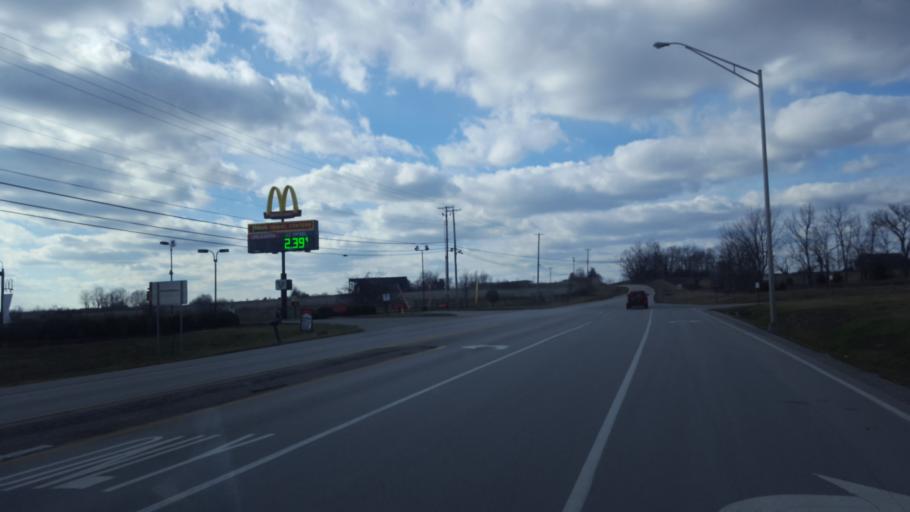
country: US
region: Kentucky
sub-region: Scott County
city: Georgetown
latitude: 38.2771
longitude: -84.5595
